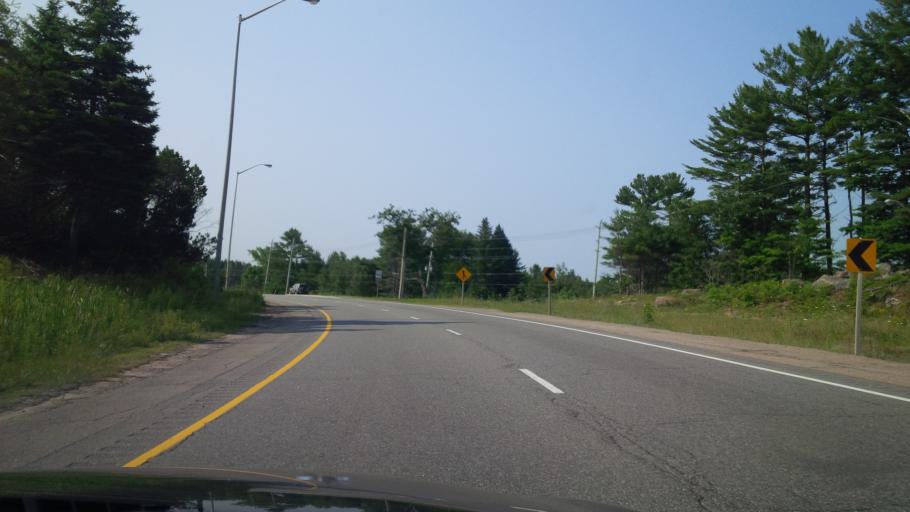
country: CA
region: Ontario
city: Gravenhurst
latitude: 44.9048
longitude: -79.3672
